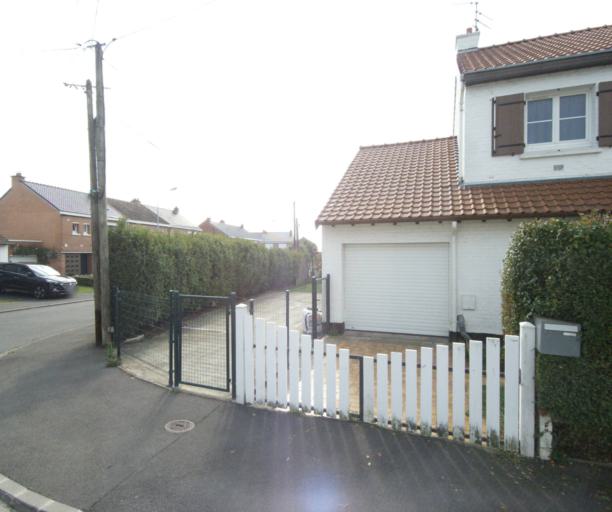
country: FR
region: Nord-Pas-de-Calais
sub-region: Departement du Nord
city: Wattignies
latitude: 50.5825
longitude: 3.0266
